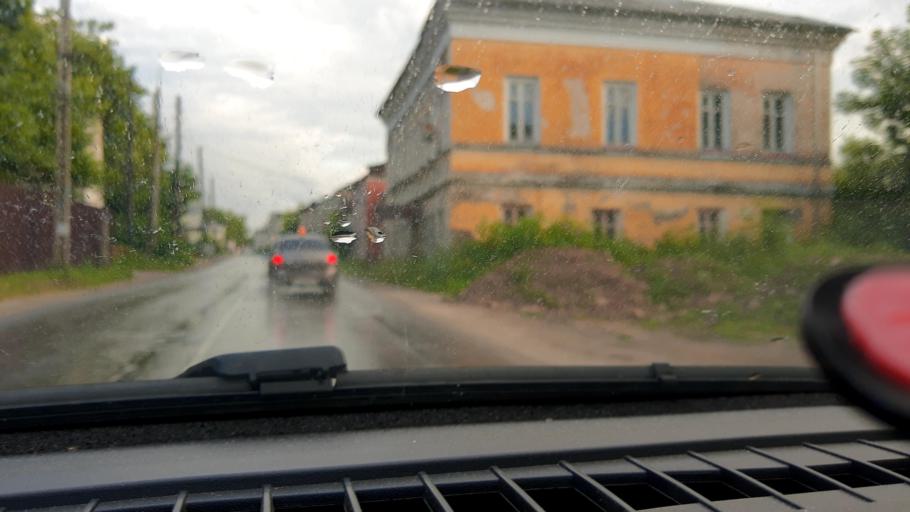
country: RU
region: Nizjnij Novgorod
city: Gorodets
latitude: 56.6474
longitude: 43.4647
